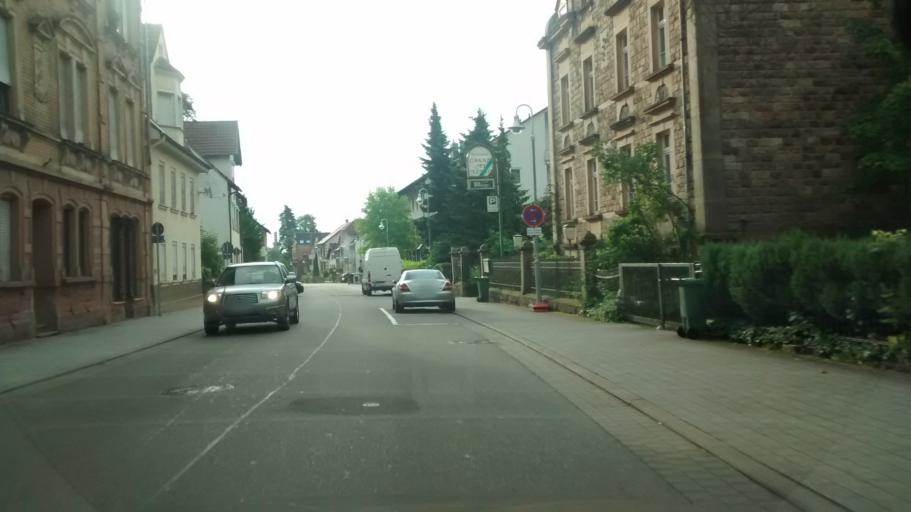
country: DE
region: Rheinland-Pfalz
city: Bad Bergzabern
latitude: 49.0996
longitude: 7.9848
